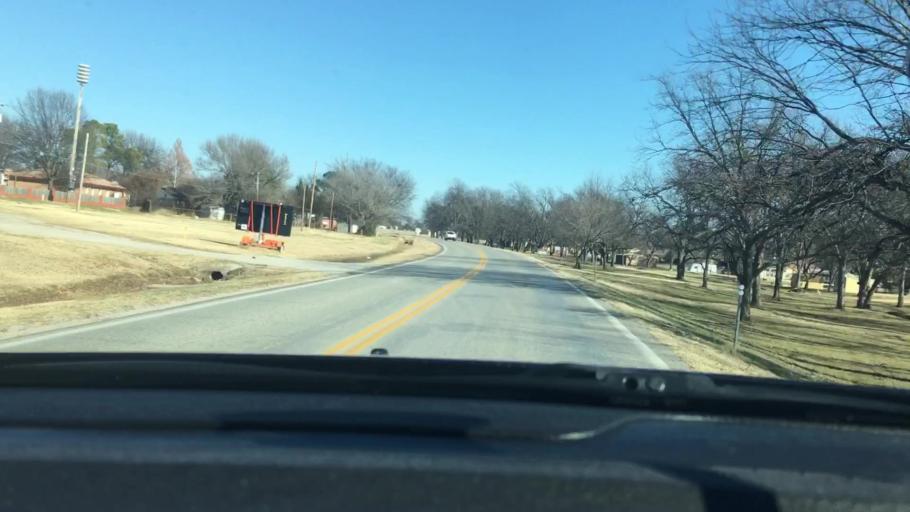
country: US
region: Oklahoma
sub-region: Garvin County
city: Wynnewood
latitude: 34.6453
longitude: -97.1551
